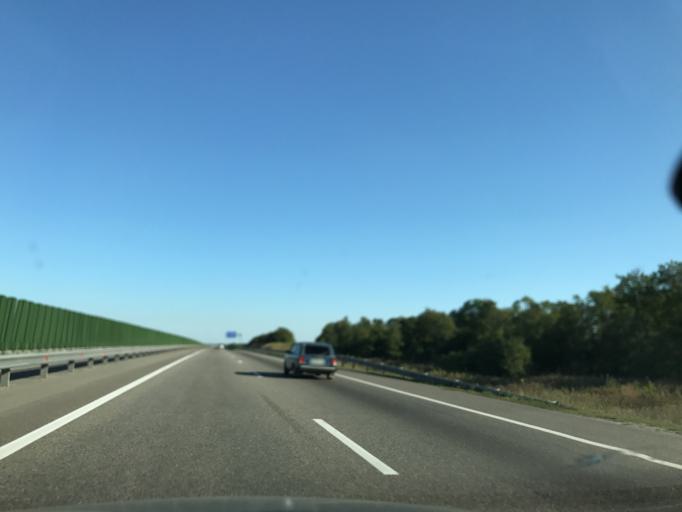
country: RU
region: Rostov
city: Glubokiy
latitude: 48.5779
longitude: 40.3521
